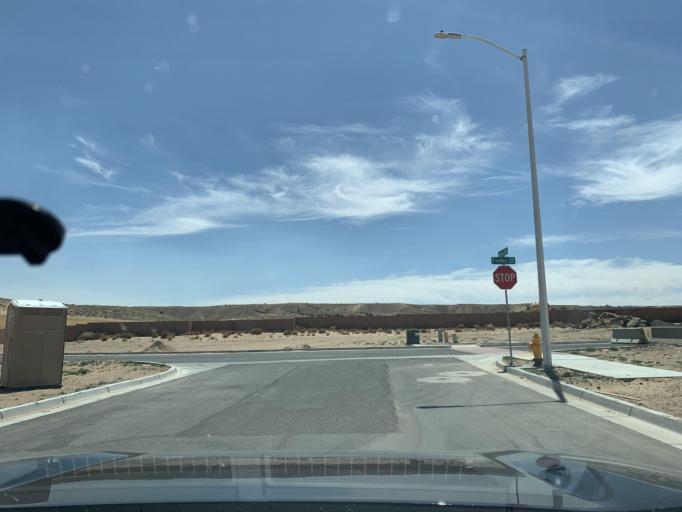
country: US
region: New Mexico
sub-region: Valencia County
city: Los Lunas
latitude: 34.8196
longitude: -106.8007
